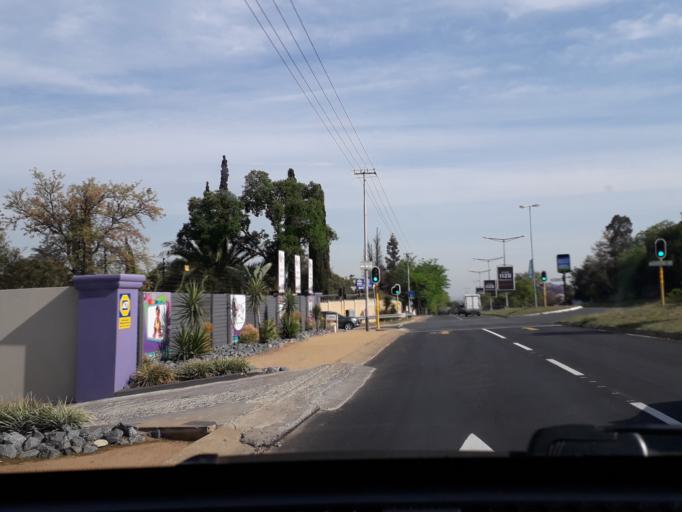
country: ZA
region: Gauteng
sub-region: City of Johannesburg Metropolitan Municipality
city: Modderfontein
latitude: -26.0731
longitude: 28.0781
